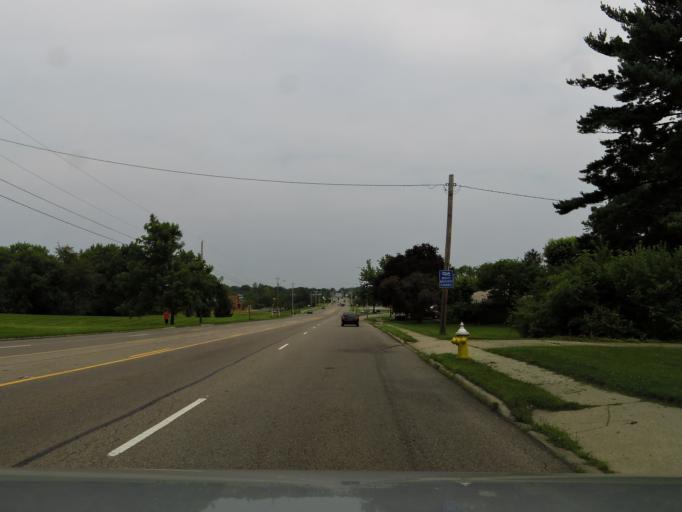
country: US
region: Ohio
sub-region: Montgomery County
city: Kettering
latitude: 39.6836
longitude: -84.1261
